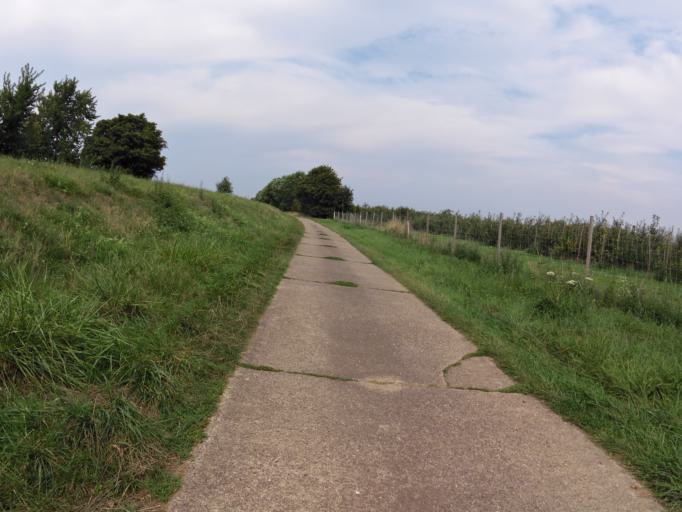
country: DE
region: Lower Saxony
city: Landesbergen
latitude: 52.5622
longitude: 9.1147
